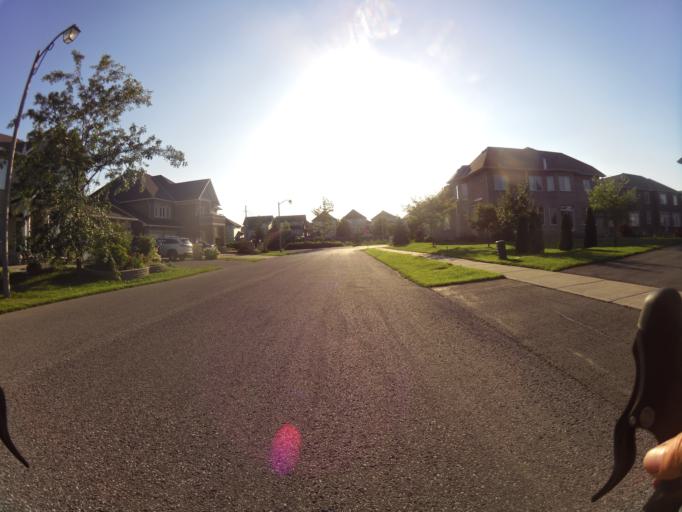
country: CA
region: Ontario
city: Ottawa
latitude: 45.2848
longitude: -75.7014
